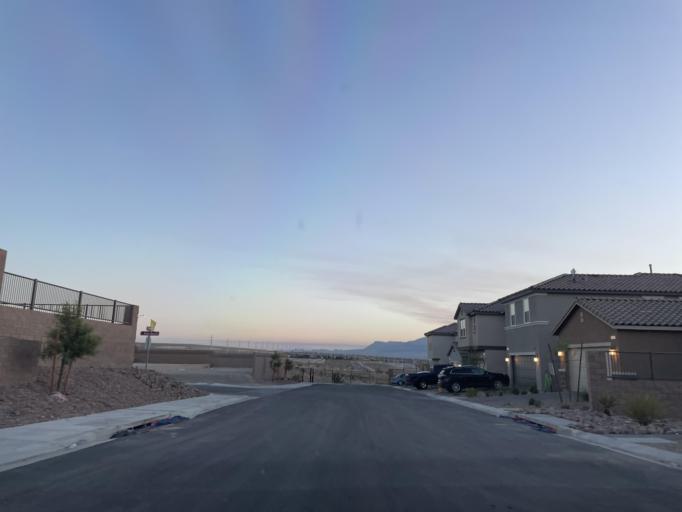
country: US
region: Nevada
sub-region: Clark County
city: Summerlin South
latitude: 36.2598
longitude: -115.3303
